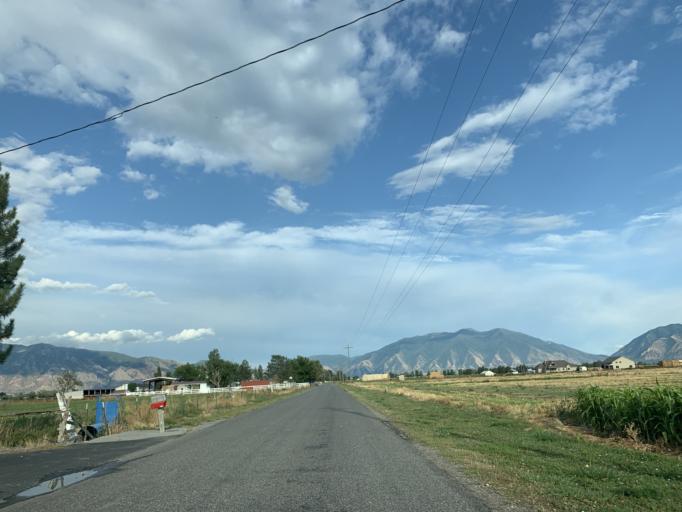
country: US
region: Utah
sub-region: Utah County
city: Benjamin
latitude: 40.1290
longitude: -111.7546
